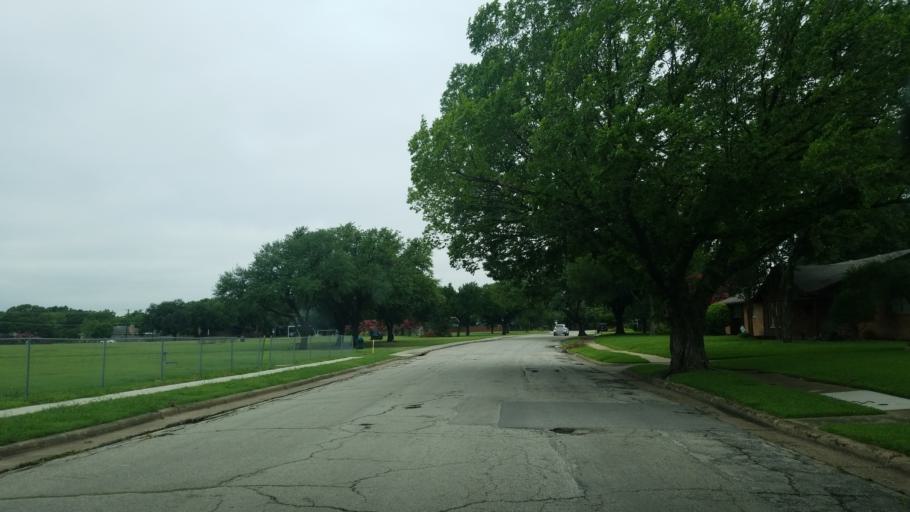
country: US
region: Texas
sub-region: Dallas County
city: Farmers Branch
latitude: 32.9051
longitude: -96.8618
